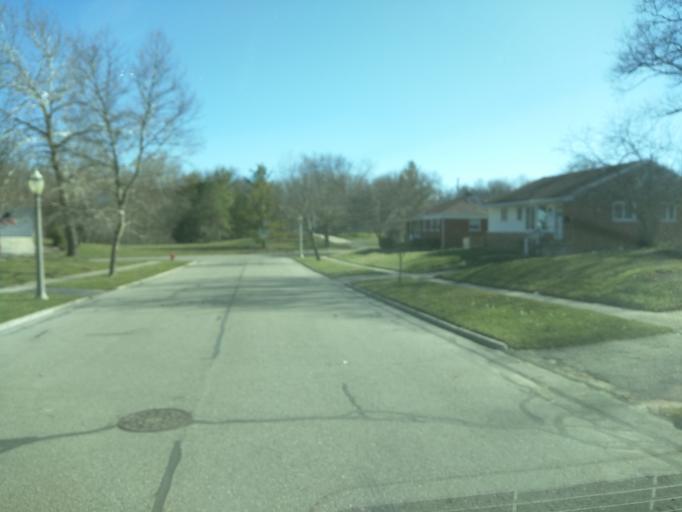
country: US
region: Michigan
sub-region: Ingham County
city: Edgemont Park
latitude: 42.7568
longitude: -84.5866
